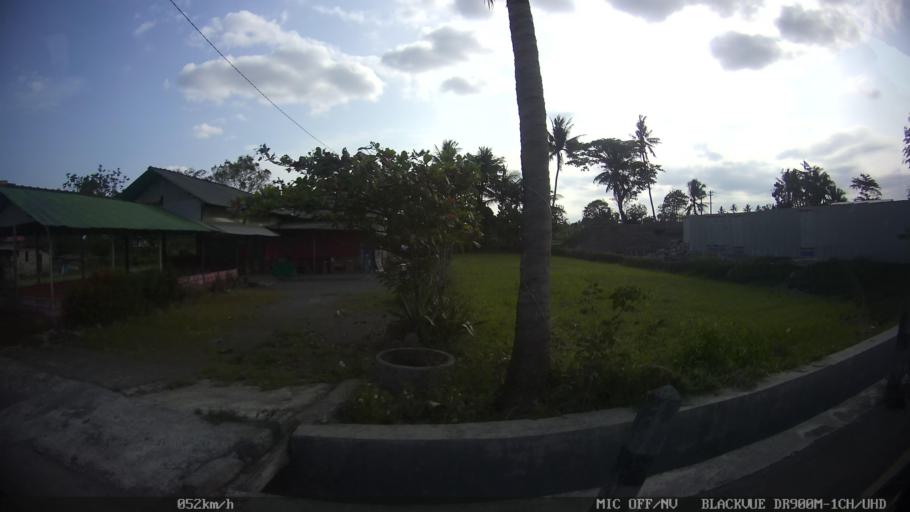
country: ID
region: Central Java
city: Candi Prambanan
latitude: -7.7112
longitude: 110.4700
